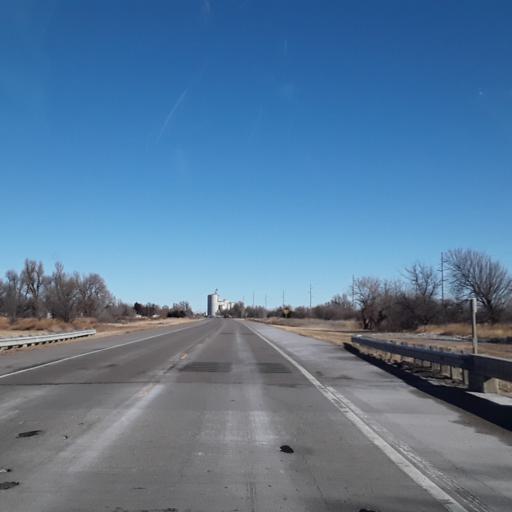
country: US
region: Kansas
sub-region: Pawnee County
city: Larned
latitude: 38.1668
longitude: -99.1118
